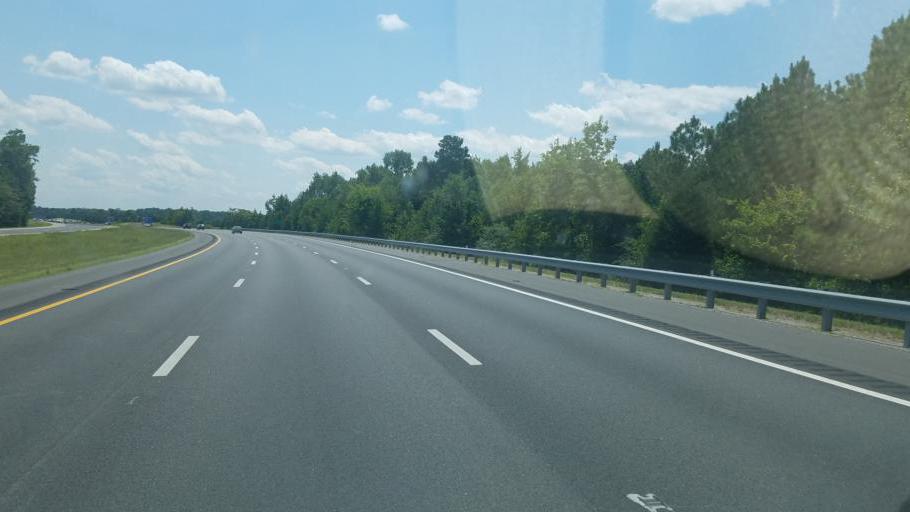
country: US
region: Virginia
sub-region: Chesterfield County
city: Enon
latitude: 37.3050
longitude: -77.3377
